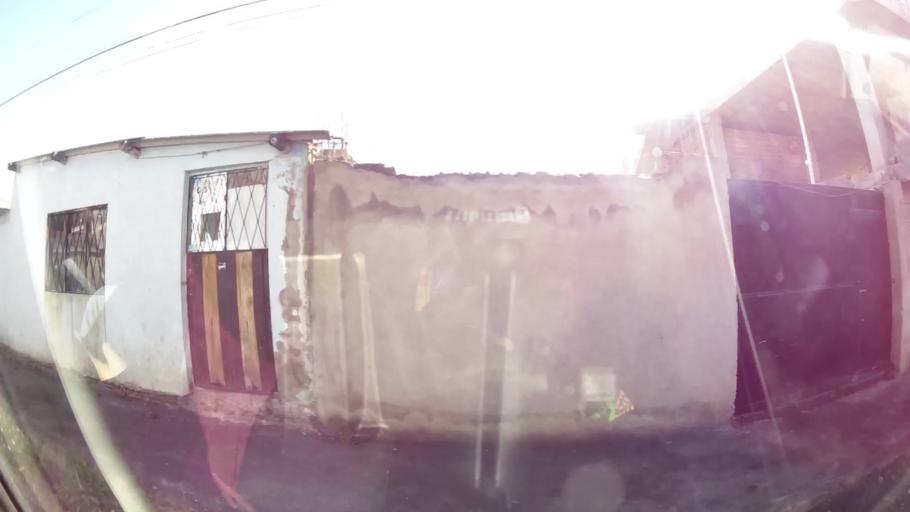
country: EC
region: Chimborazo
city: Riobamba
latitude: -1.6507
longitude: -78.6746
